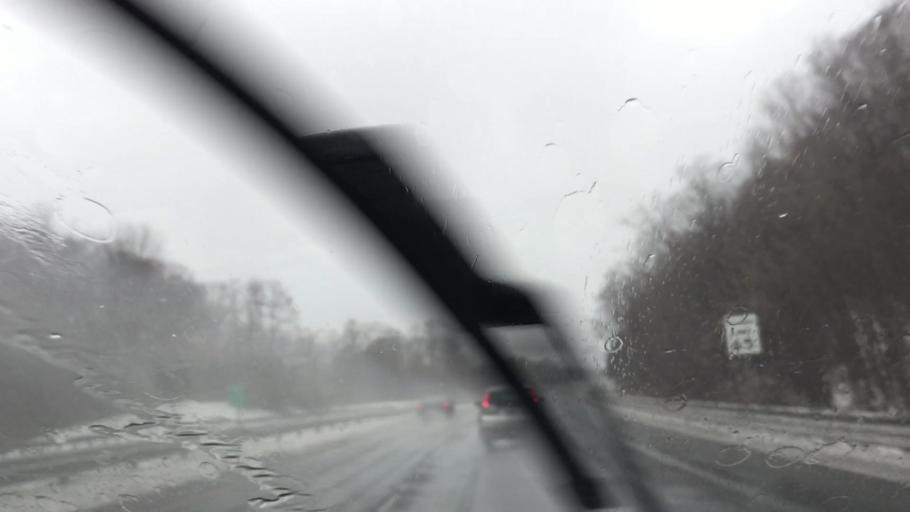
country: US
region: Massachusetts
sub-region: Hampden County
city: Granville
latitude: 42.1707
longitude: -72.8912
